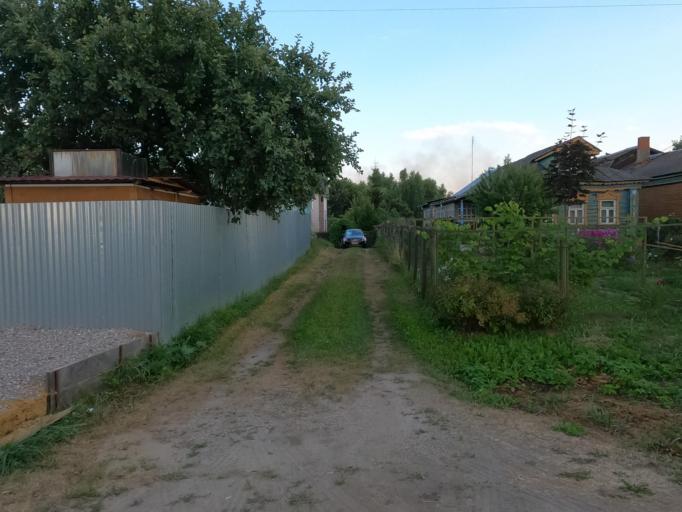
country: RU
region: Moskovskaya
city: Ashitkovo
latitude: 55.4226
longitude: 38.5872
